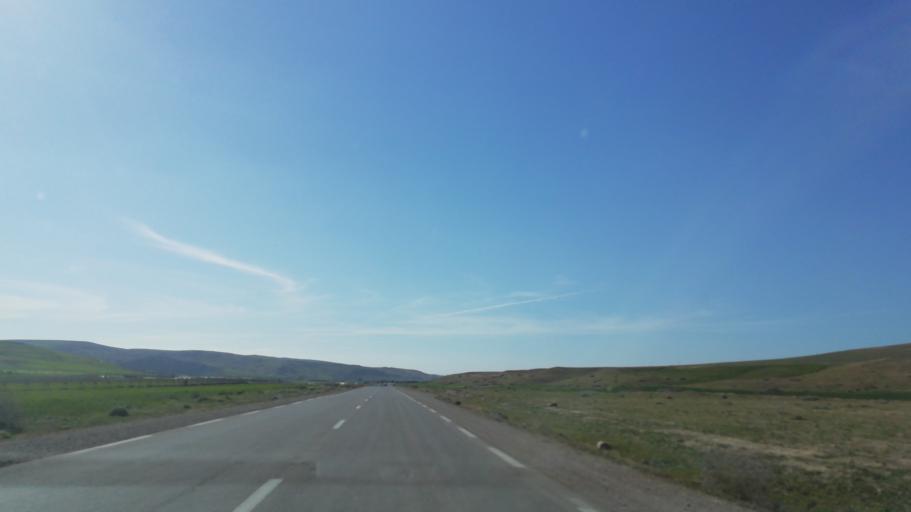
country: DZ
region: Mascara
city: Oued el Abtal
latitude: 35.4498
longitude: 0.7996
